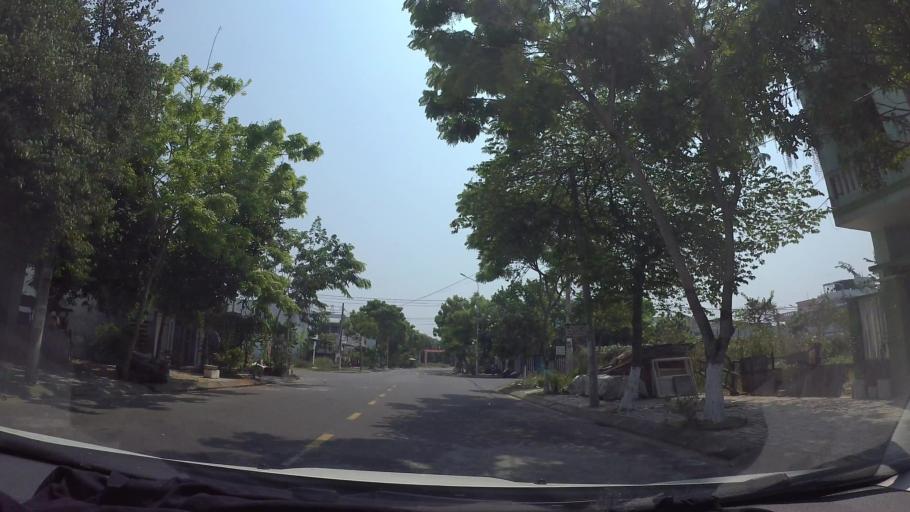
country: VN
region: Da Nang
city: Cam Le
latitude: 15.9970
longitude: 108.2047
